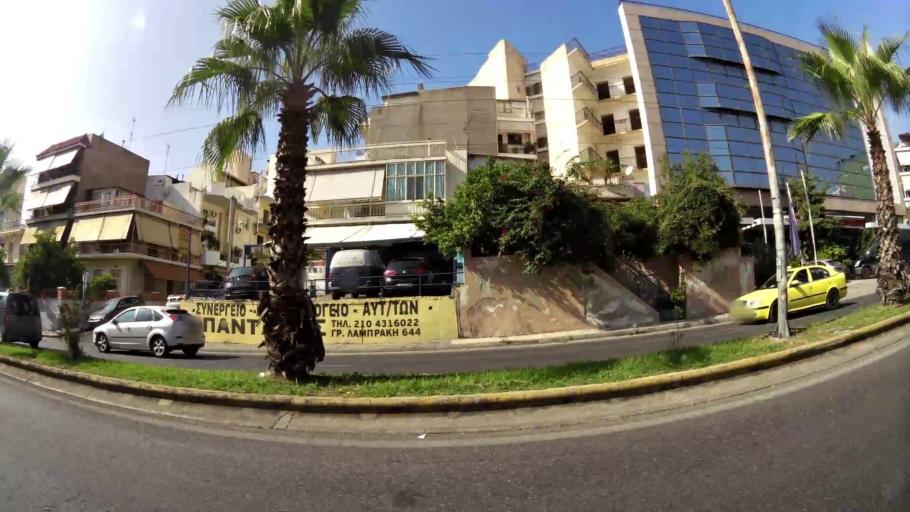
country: GR
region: Attica
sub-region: Nomos Piraios
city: Keratsini
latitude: 37.9670
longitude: 23.6168
